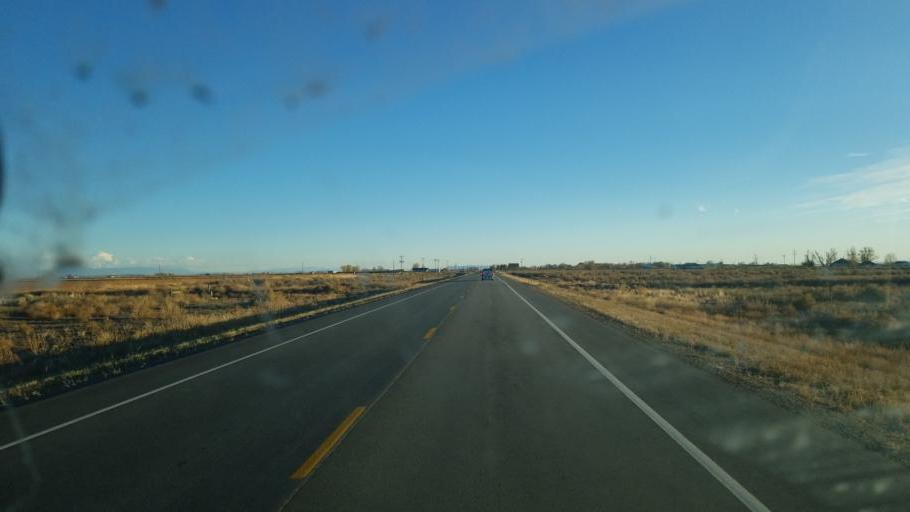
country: US
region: Colorado
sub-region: Alamosa County
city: Alamosa East
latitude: 37.6670
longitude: -105.8719
